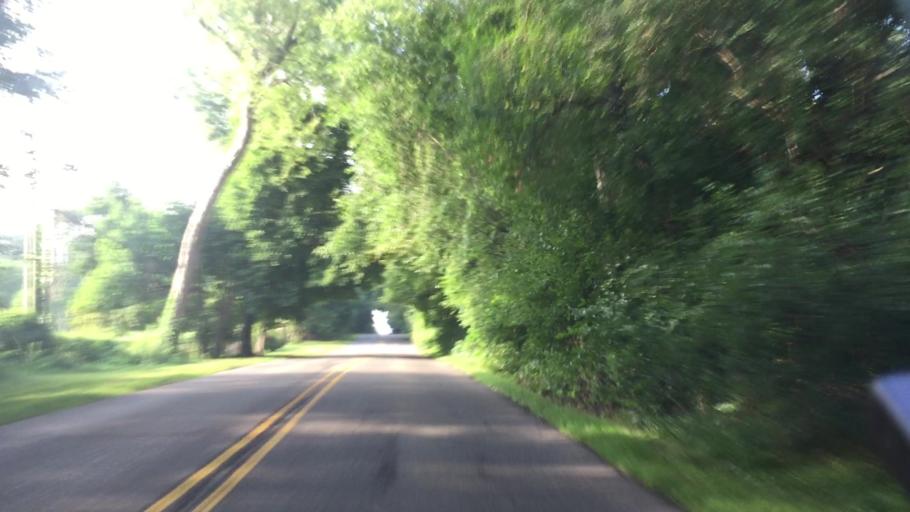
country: US
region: Michigan
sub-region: Oakland County
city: Bloomfield Hills
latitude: 42.5909
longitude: -83.2474
